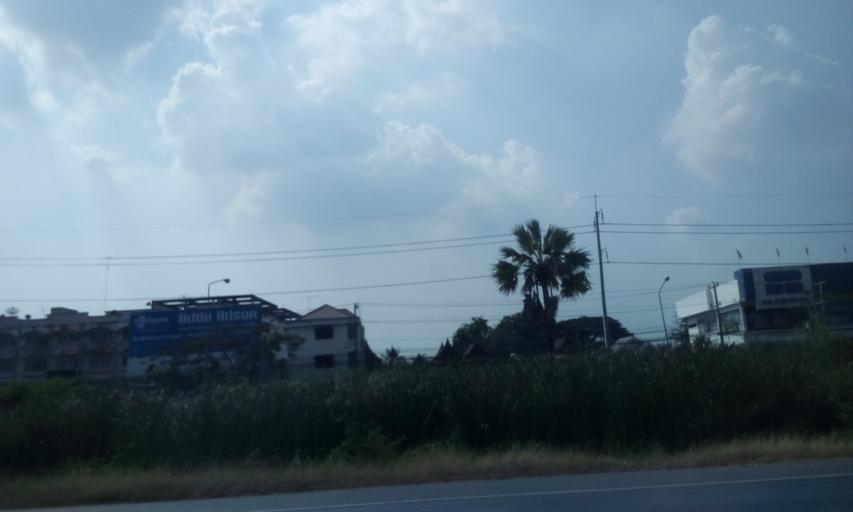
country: TH
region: Phra Nakhon Si Ayutthaya
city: Phra Nakhon Si Ayutthaya
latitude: 14.3532
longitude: 100.6130
